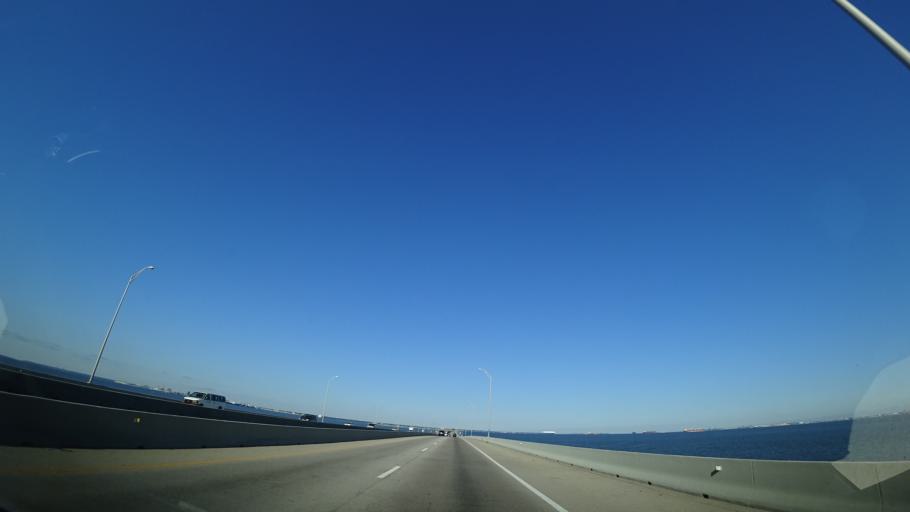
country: US
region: Virginia
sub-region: City of Newport News
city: Newport News
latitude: 36.9199
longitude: -76.4130
